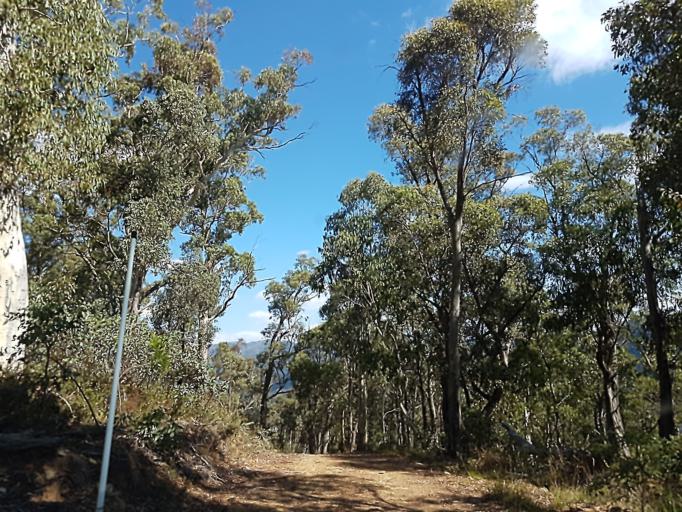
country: AU
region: Victoria
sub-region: Alpine
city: Mount Beauty
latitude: -36.8899
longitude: 147.0260
